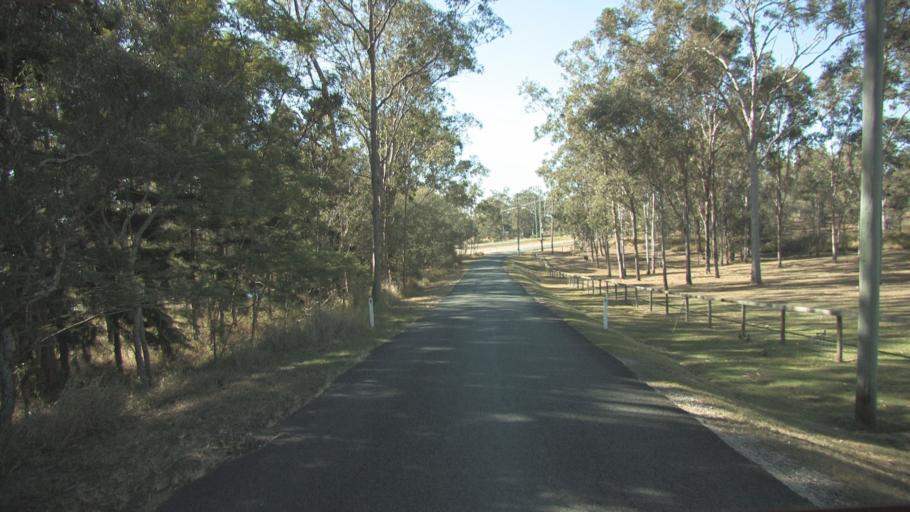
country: AU
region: Queensland
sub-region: Logan
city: North Maclean
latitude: -27.7909
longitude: 153.0140
